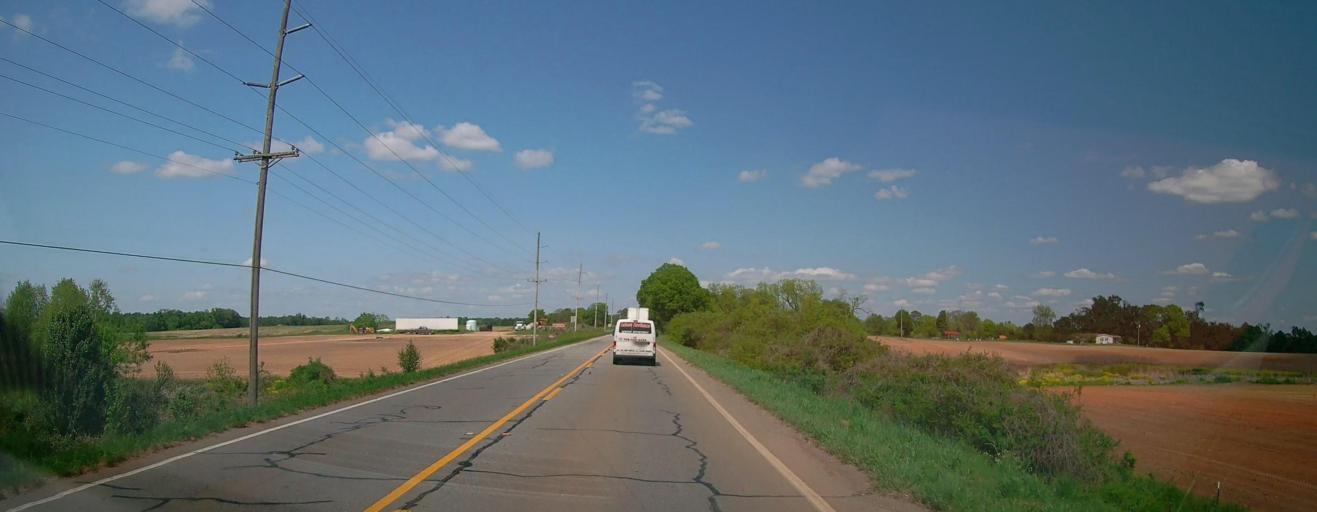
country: US
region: Georgia
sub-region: Putnam County
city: Eatonton
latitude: 33.3471
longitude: -83.3575
